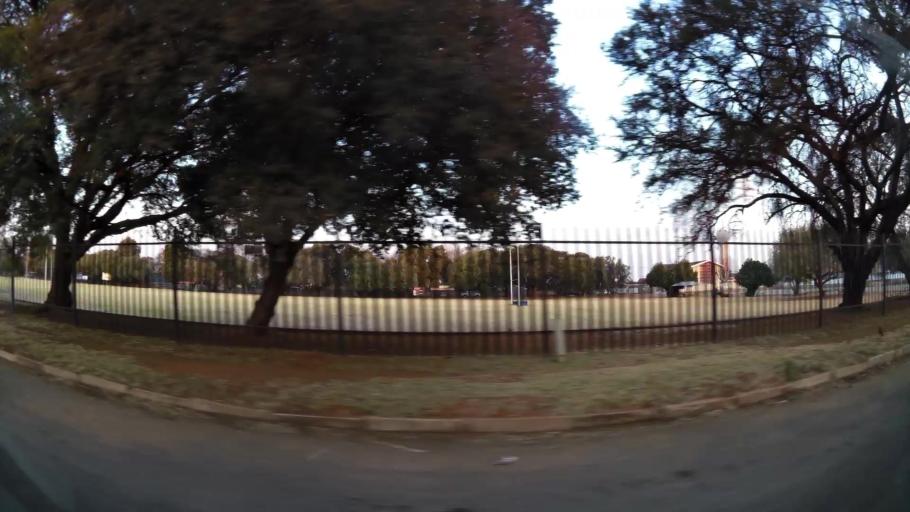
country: ZA
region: Gauteng
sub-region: Ekurhuleni Metropolitan Municipality
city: Tembisa
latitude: -26.0597
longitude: 28.2315
